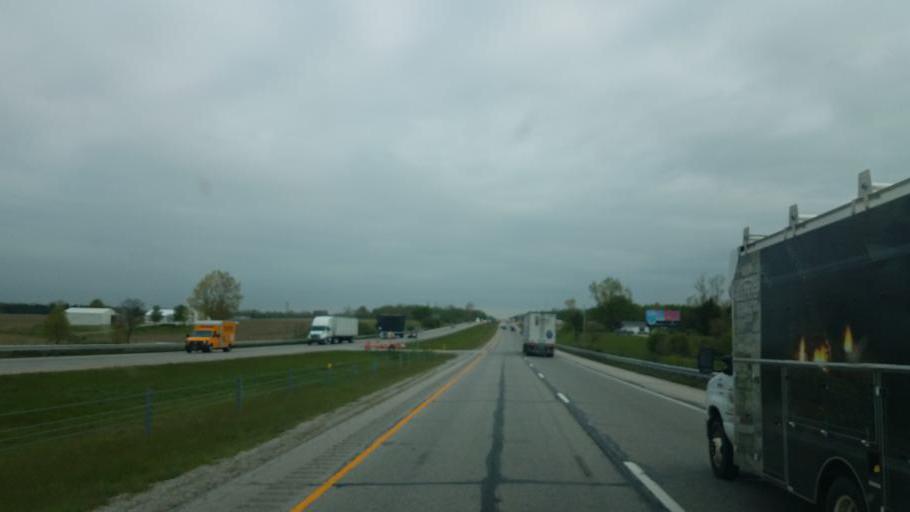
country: US
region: Indiana
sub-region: DeKalb County
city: Garrett
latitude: 41.2856
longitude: -85.0871
